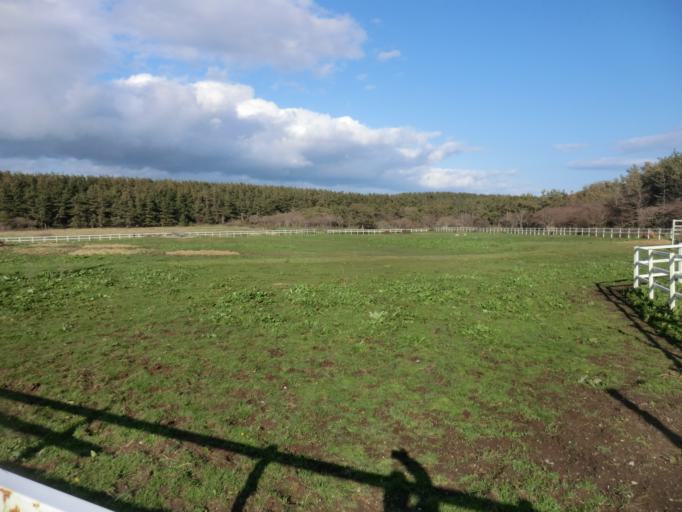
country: JP
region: Aomori
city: Mutsu
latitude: 41.4128
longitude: 141.4480
